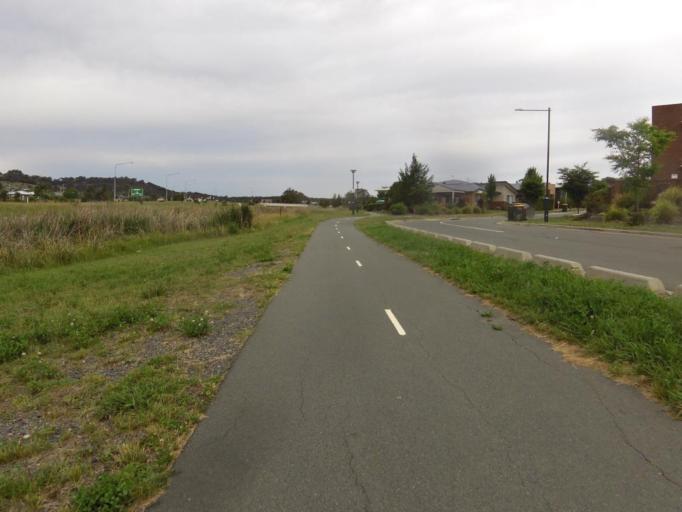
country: AU
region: Australian Capital Territory
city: Kaleen
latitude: -35.1613
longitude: 149.1467
